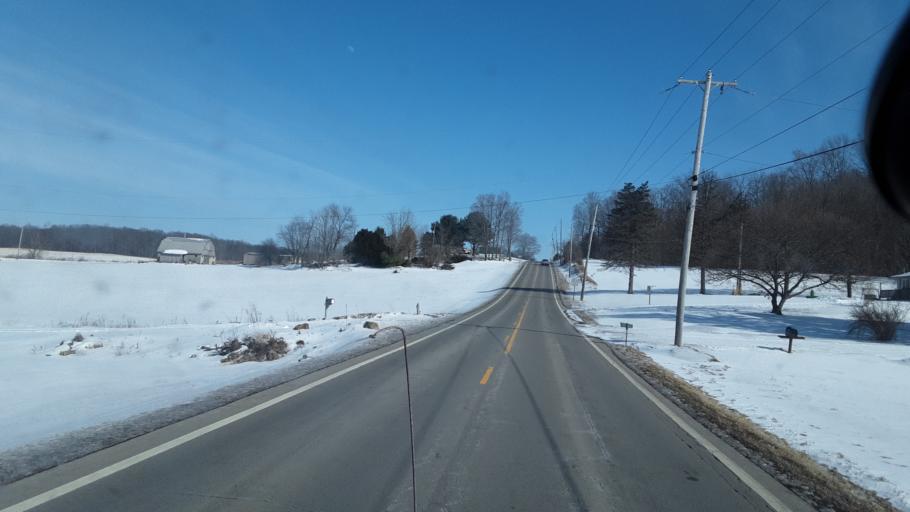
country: US
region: Ohio
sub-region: Columbiana County
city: Salem
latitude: 40.9442
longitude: -80.8238
